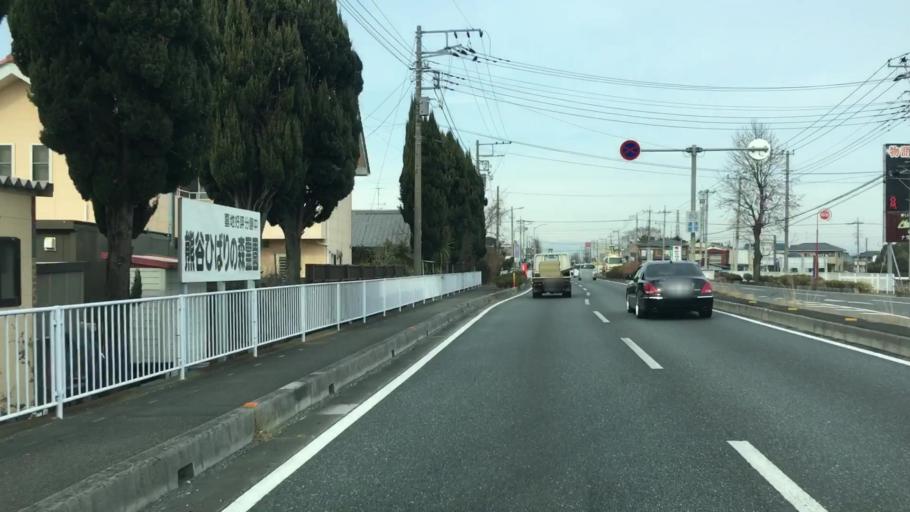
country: JP
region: Saitama
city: Kumagaya
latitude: 36.1626
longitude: 139.3707
